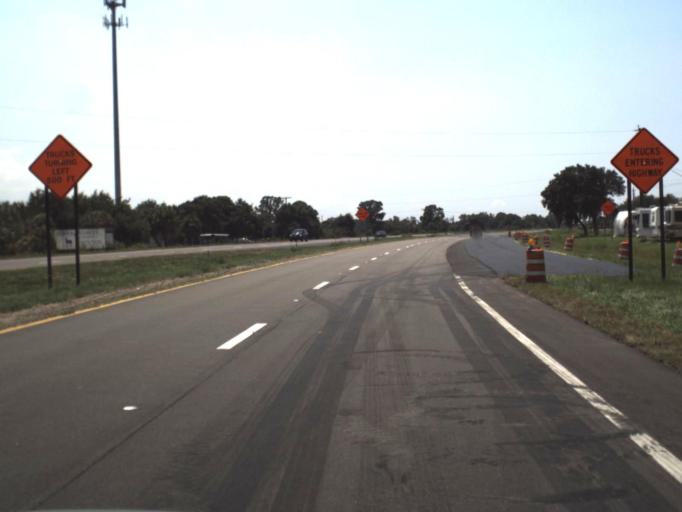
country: US
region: Florida
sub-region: Hillsborough County
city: Ruskin
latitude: 27.6754
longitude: -82.4796
